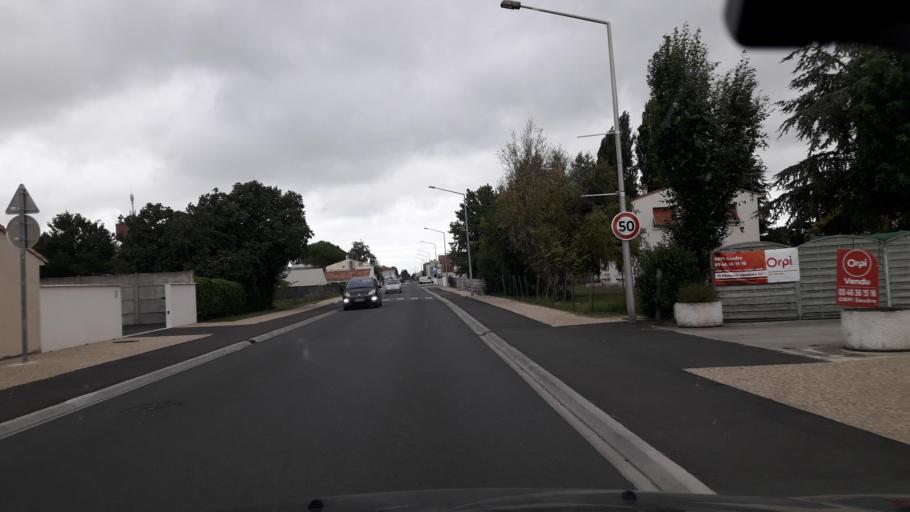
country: FR
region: Poitou-Charentes
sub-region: Departement de la Charente-Maritime
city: Arvert
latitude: 45.7415
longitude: -1.1192
